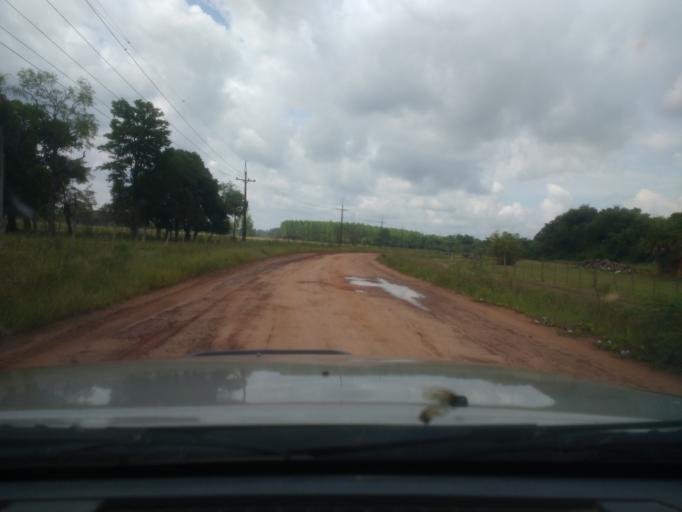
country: PY
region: San Pedro
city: Puerto Rosario
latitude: -24.3937
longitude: -57.1044
